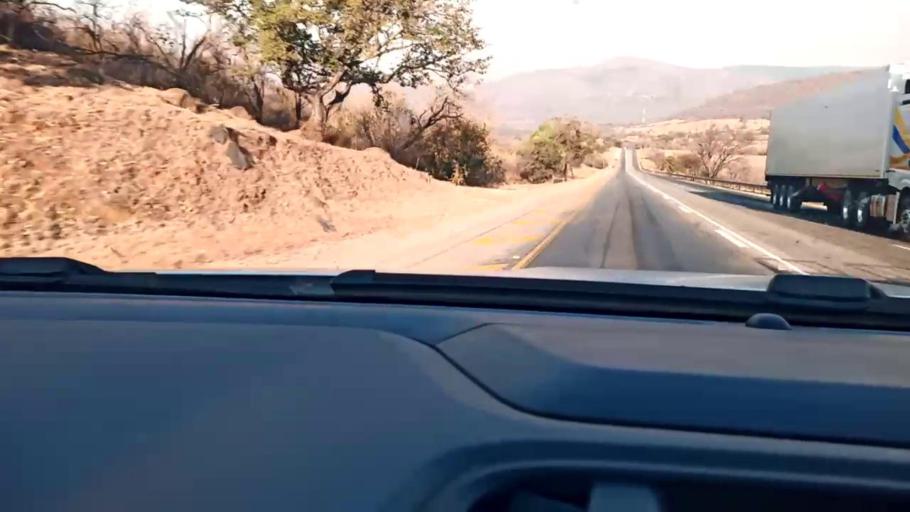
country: ZA
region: Limpopo
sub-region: Mopani District Municipality
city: Duiwelskloof
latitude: -23.6385
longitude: 30.1530
